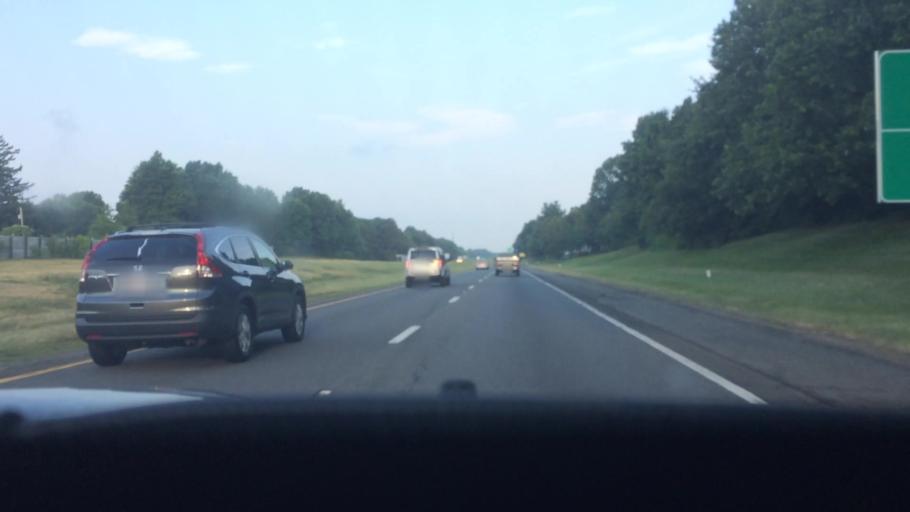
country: US
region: Massachusetts
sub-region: Hampden County
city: Ludlow
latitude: 42.1642
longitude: -72.5109
